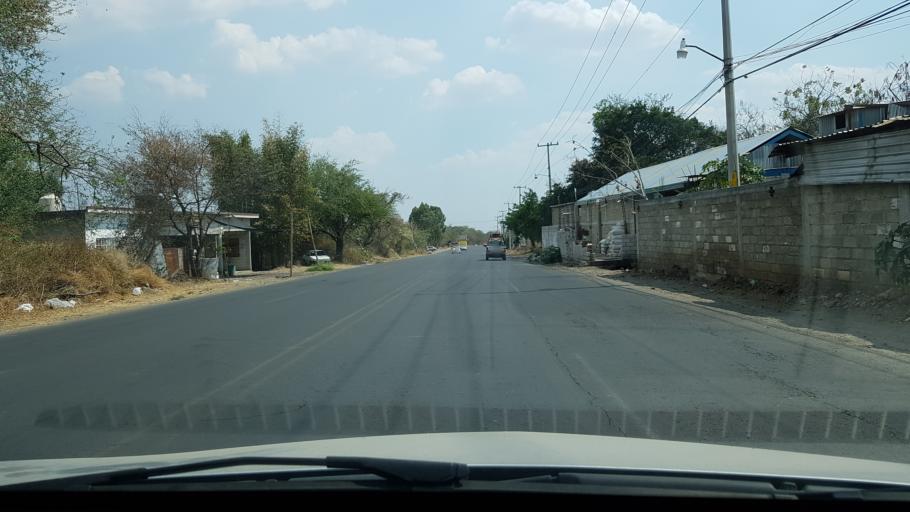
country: MX
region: Morelos
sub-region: Temoac
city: Huazulco
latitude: 18.7593
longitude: -98.7796
